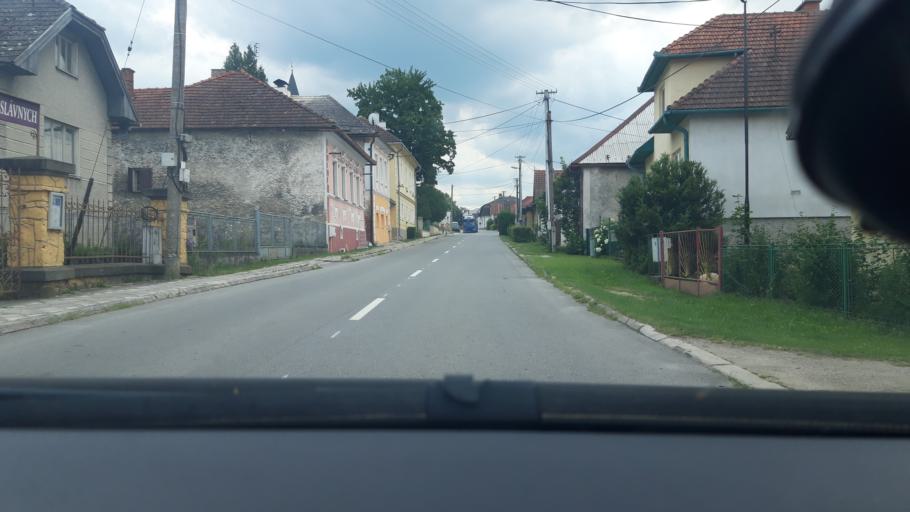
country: SK
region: Zilinsky
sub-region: Okres Martin
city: Martin
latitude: 48.9121
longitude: 18.8858
